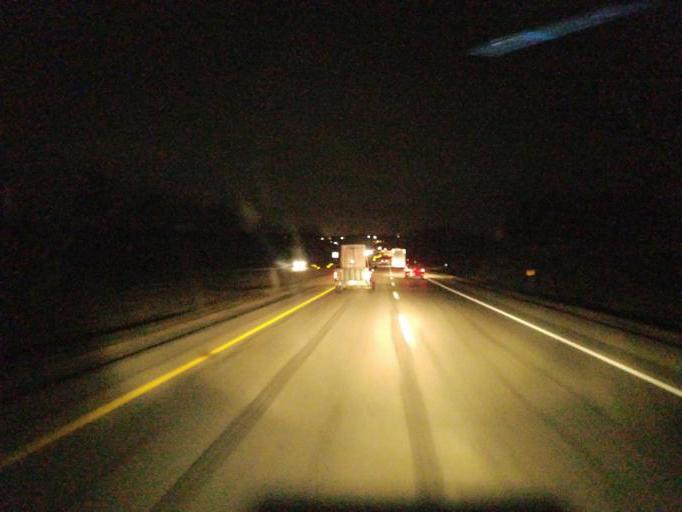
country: US
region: Iowa
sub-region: Dallas County
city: Van Meter
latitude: 41.5445
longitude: -93.9723
